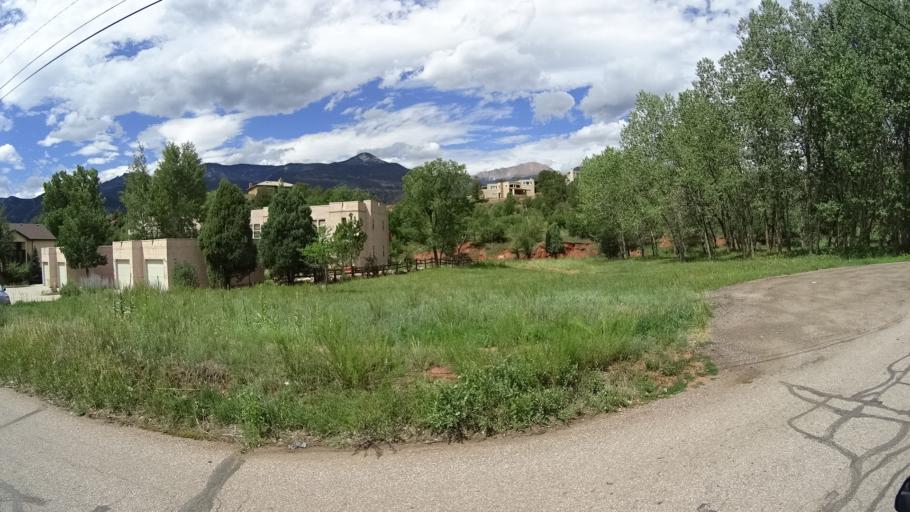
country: US
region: Colorado
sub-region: El Paso County
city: Manitou Springs
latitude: 38.8626
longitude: -104.8924
